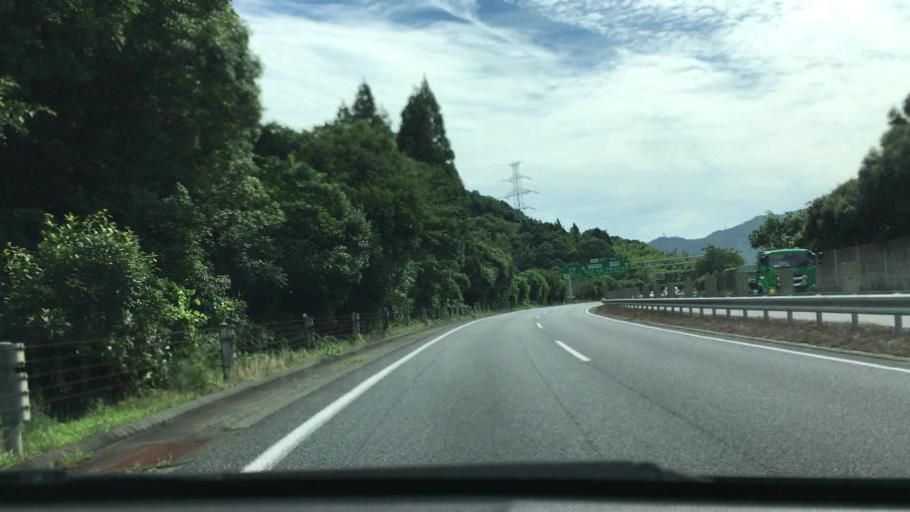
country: JP
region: Yamaguchi
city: Ogori-shimogo
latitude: 34.1247
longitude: 131.4191
